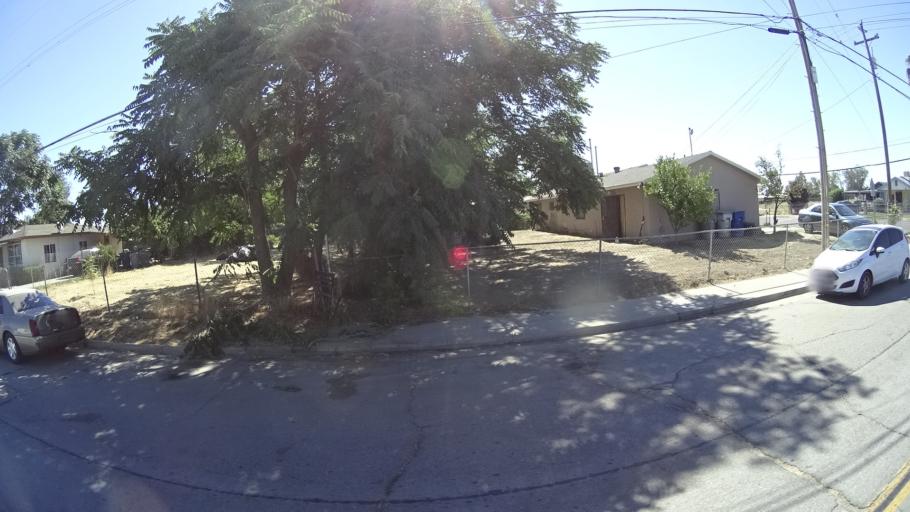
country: US
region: California
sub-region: Fresno County
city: Easton
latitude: 36.6926
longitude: -119.7946
